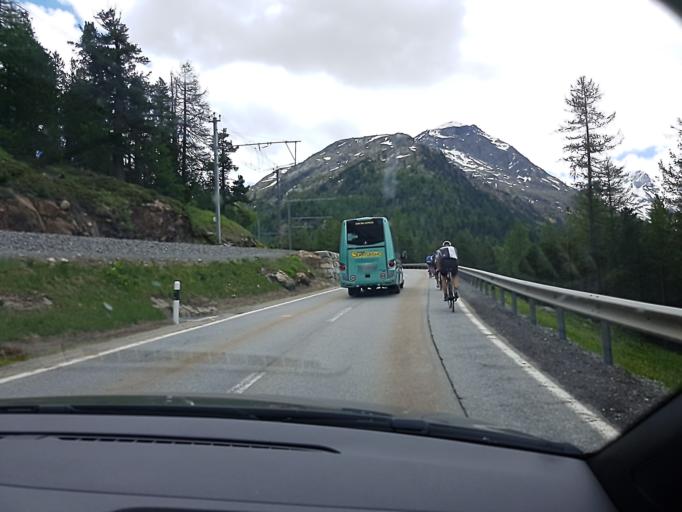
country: CH
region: Grisons
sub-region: Maloja District
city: Pontresina
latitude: 46.4561
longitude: 9.9445
